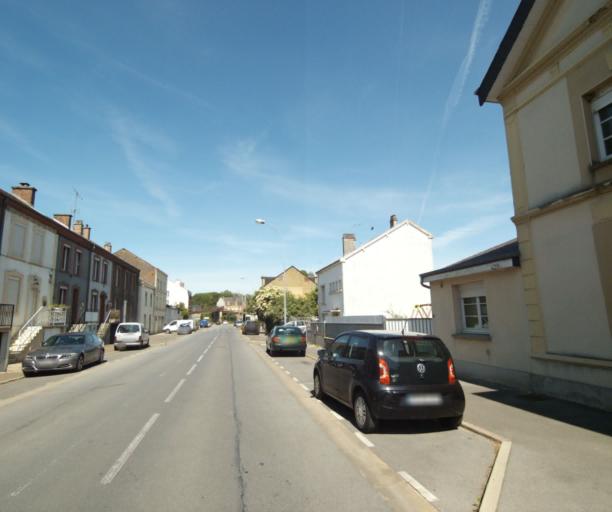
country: FR
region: Champagne-Ardenne
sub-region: Departement des Ardennes
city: Villers-Semeuse
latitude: 49.7440
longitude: 4.7373
